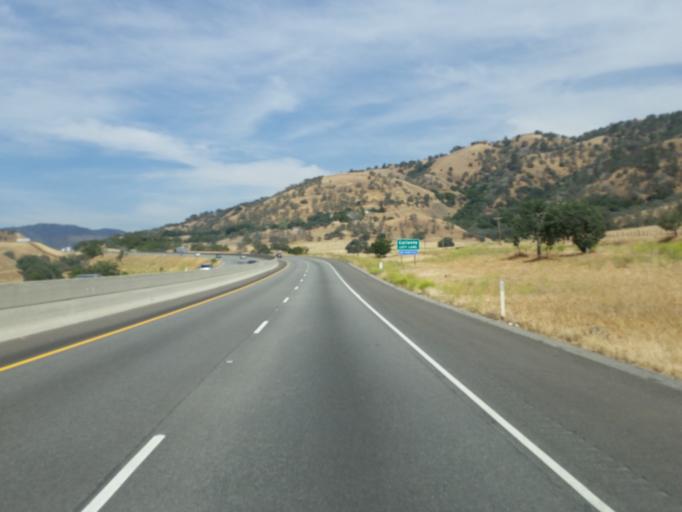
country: US
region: California
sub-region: Kern County
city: Bear Valley Springs
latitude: 35.2635
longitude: -118.6446
